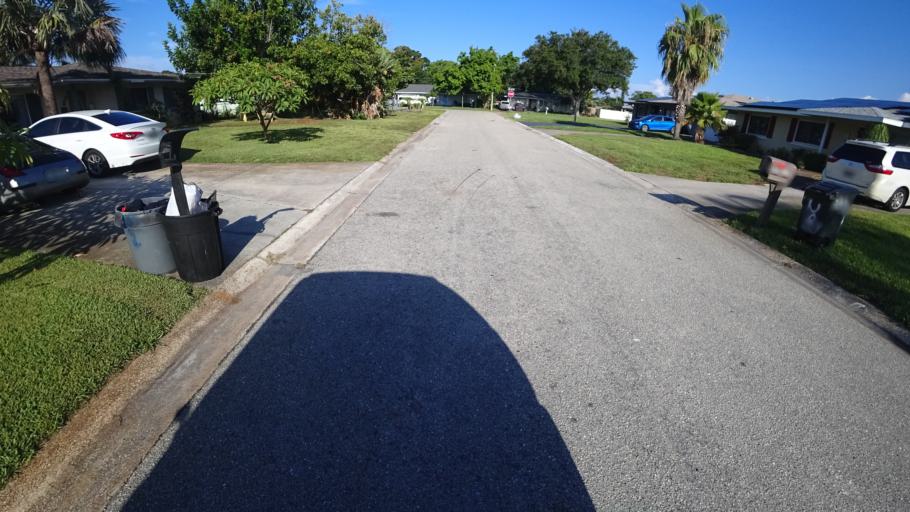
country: US
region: Florida
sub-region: Manatee County
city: South Bradenton
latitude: 27.4768
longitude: -82.5912
